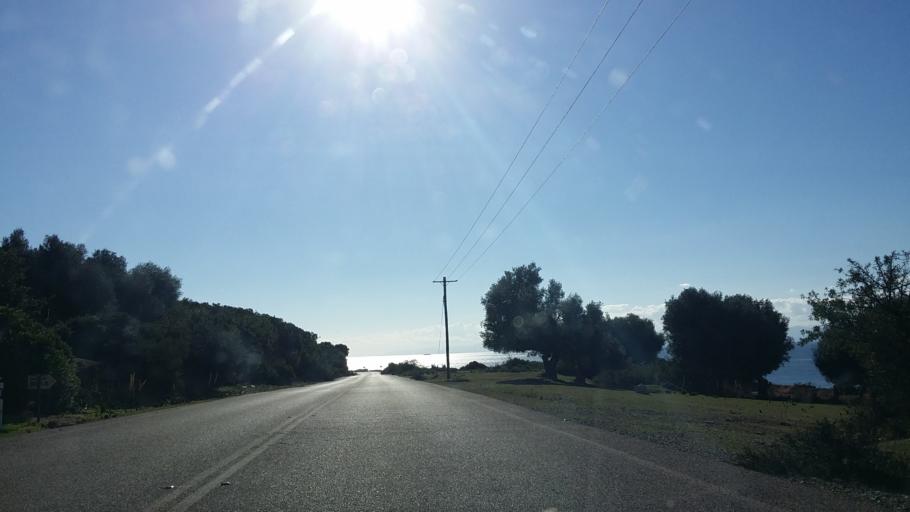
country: GR
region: West Greece
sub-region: Nomos Aitolias kai Akarnanias
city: Astakos
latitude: 38.5807
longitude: 21.0224
